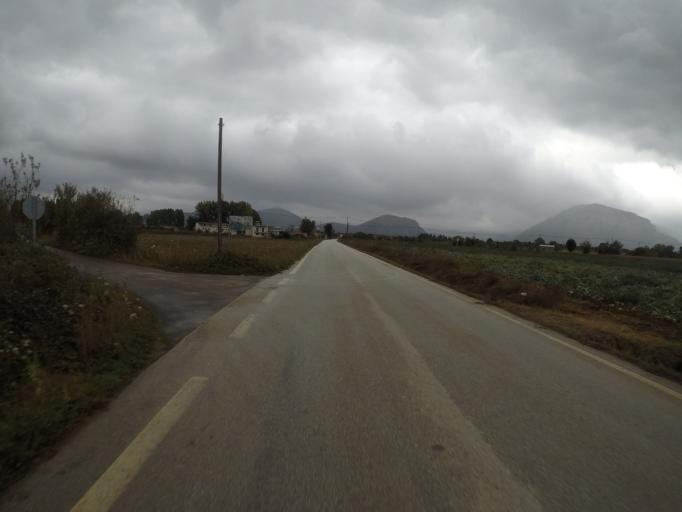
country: GR
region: Peloponnese
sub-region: Nomos Arkadias
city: Tripoli
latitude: 37.5705
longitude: 22.4101
